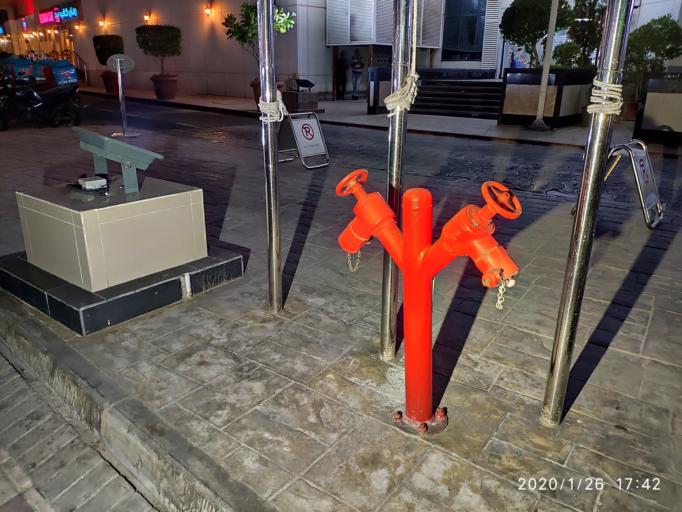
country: QA
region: Baladiyat ad Dawhah
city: Doha
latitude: 25.3177
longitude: 51.5214
